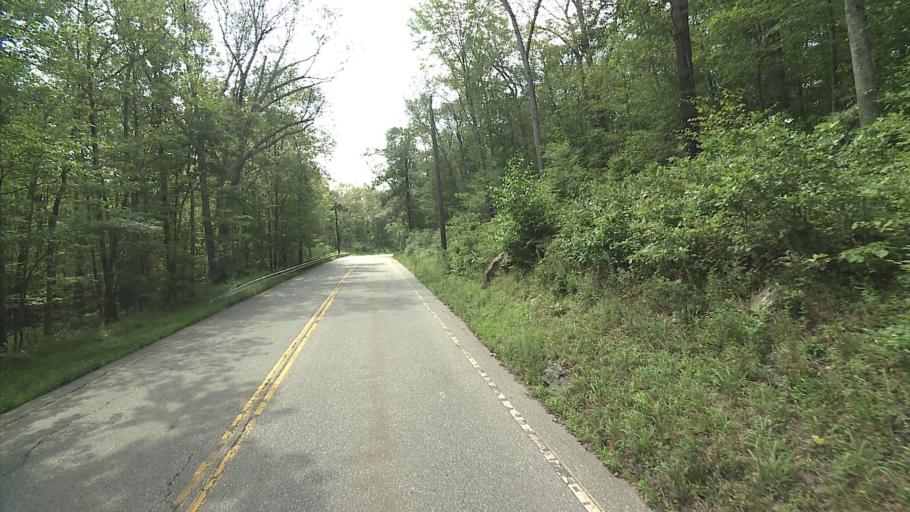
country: US
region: Connecticut
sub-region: New London County
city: Colchester
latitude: 41.4550
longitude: -72.3071
